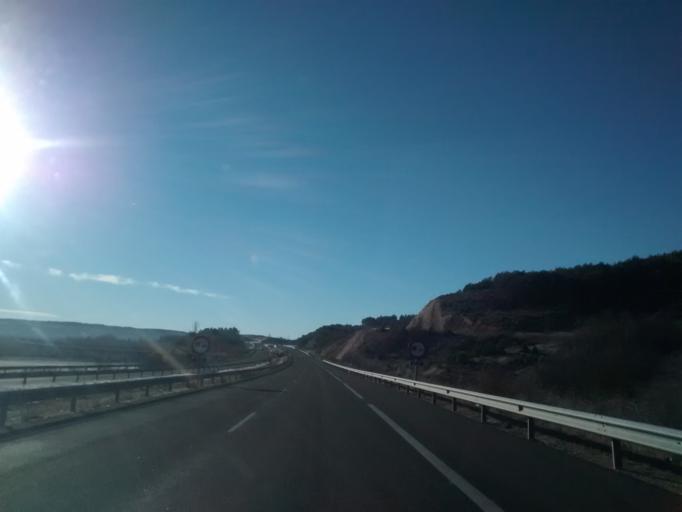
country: ES
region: Castille and Leon
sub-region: Provincia de Palencia
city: Aguilar de Campoo
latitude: 42.7377
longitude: -4.2894
